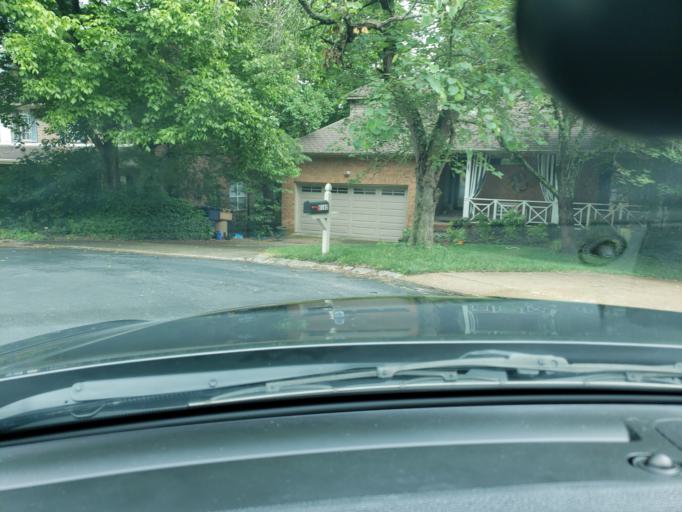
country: US
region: Tennessee
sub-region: Williamson County
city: Nolensville
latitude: 36.0358
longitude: -86.6836
